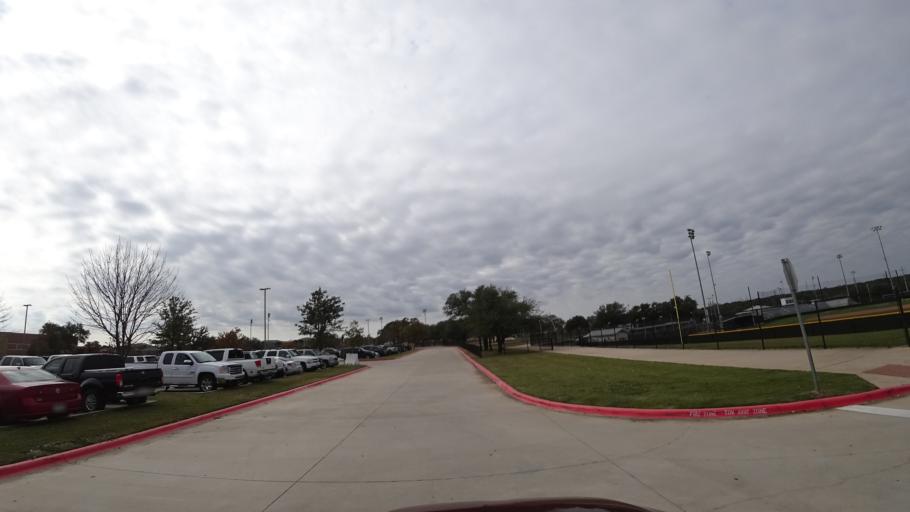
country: US
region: Texas
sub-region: Williamson County
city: Anderson Mill
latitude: 30.3989
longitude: -97.8259
